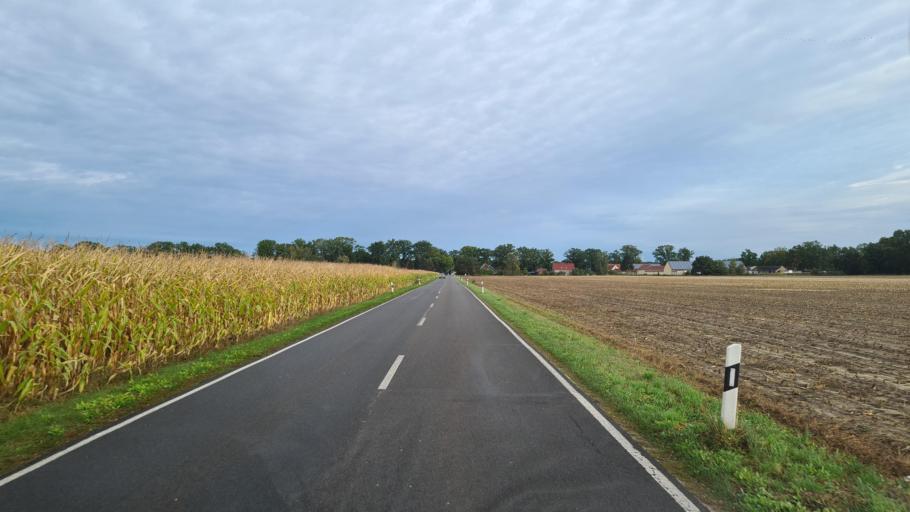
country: DE
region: Brandenburg
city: Kasel-Golzig
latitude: 51.9292
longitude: 13.7075
